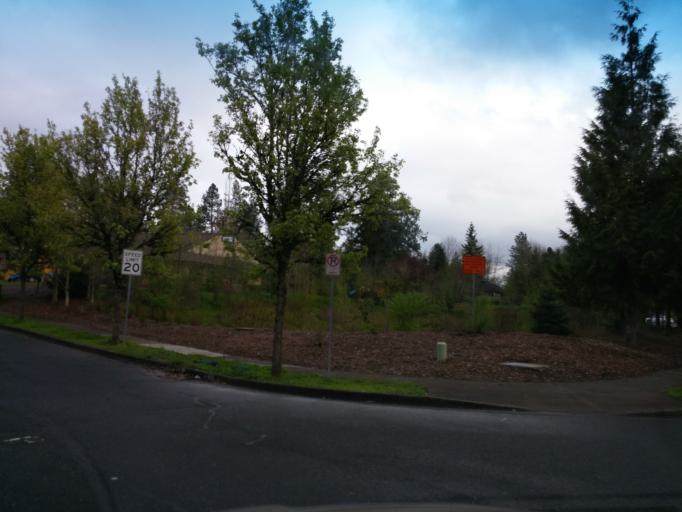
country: US
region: Oregon
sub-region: Washington County
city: Oak Hills
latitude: 45.5173
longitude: -122.8444
